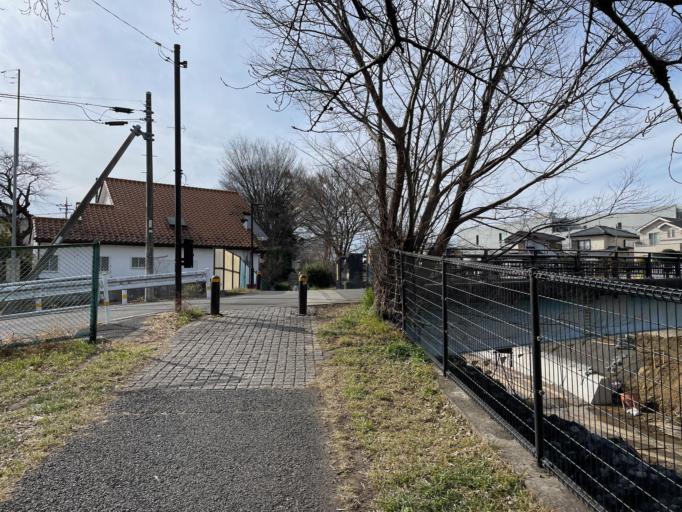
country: JP
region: Saitama
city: Tokorozawa
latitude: 35.7783
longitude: 139.5060
